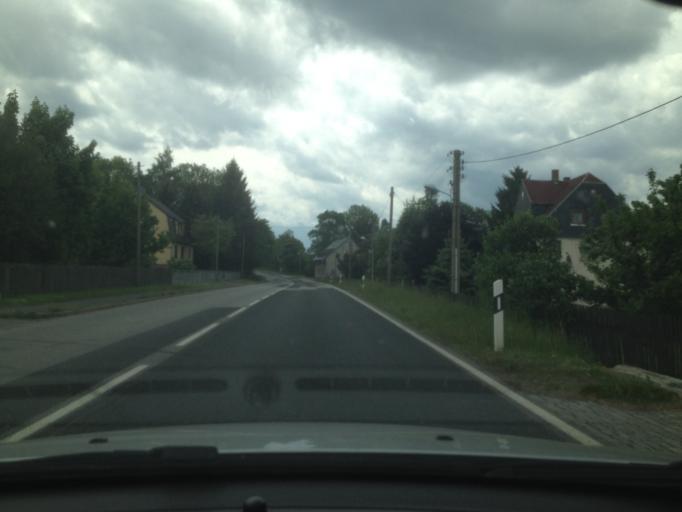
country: DE
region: Saxony
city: Lossnitz
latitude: 50.6592
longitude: 12.7545
